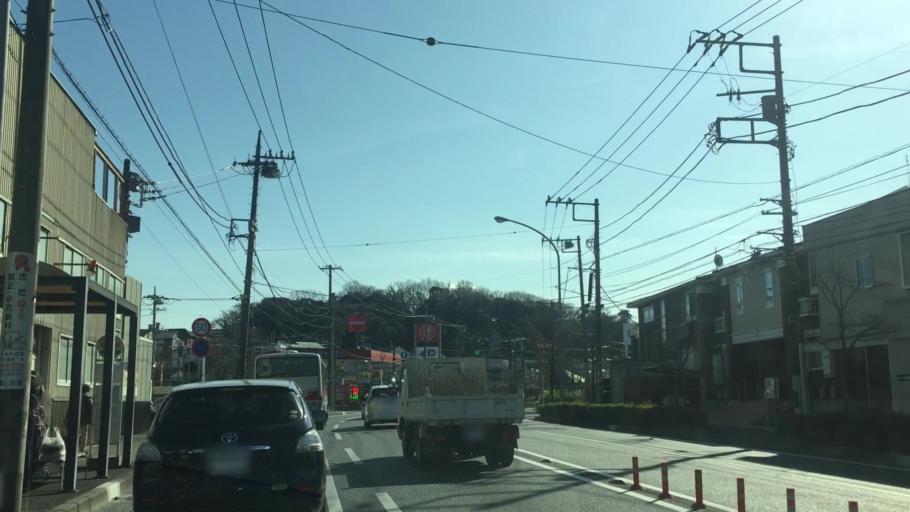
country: JP
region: Kanagawa
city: Yokohama
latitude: 35.3692
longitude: 139.6132
